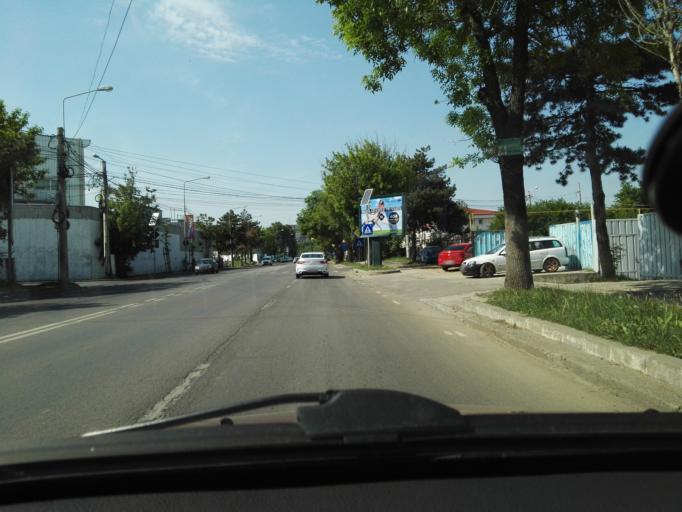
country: RO
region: Ilfov
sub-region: Comuna Popesti-Leordeni
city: Popesti-Leordeni
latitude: 44.3738
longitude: 26.1219
